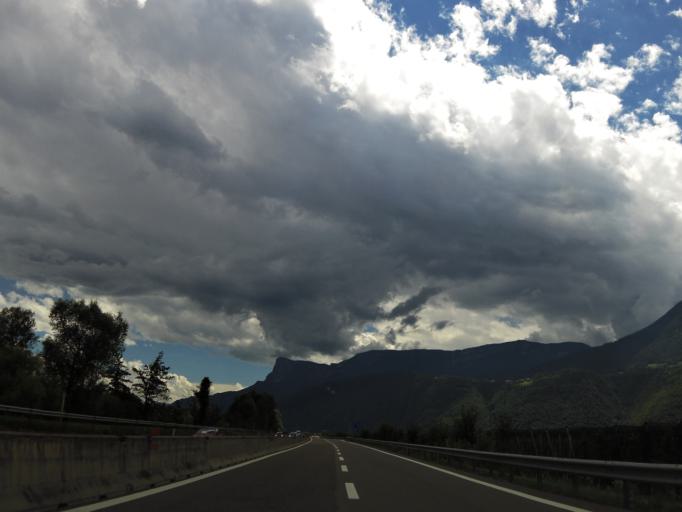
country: IT
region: Trentino-Alto Adige
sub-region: Bolzano
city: Gargazzone
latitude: 46.5930
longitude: 11.1864
